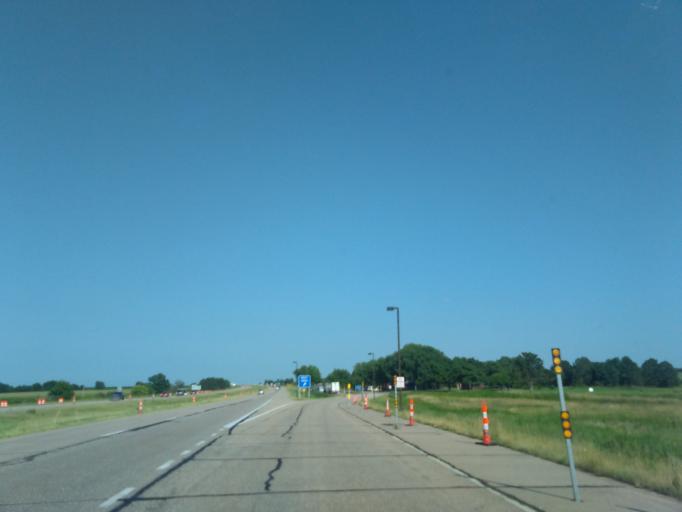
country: US
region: Nebraska
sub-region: Hall County
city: Grand Island
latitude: 40.8240
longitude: -98.3297
